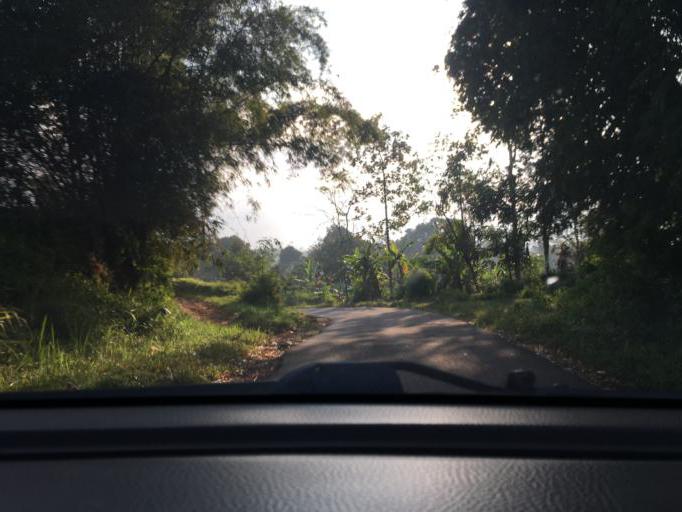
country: ID
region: West Java
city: Maniis
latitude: -7.0365
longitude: 108.3220
